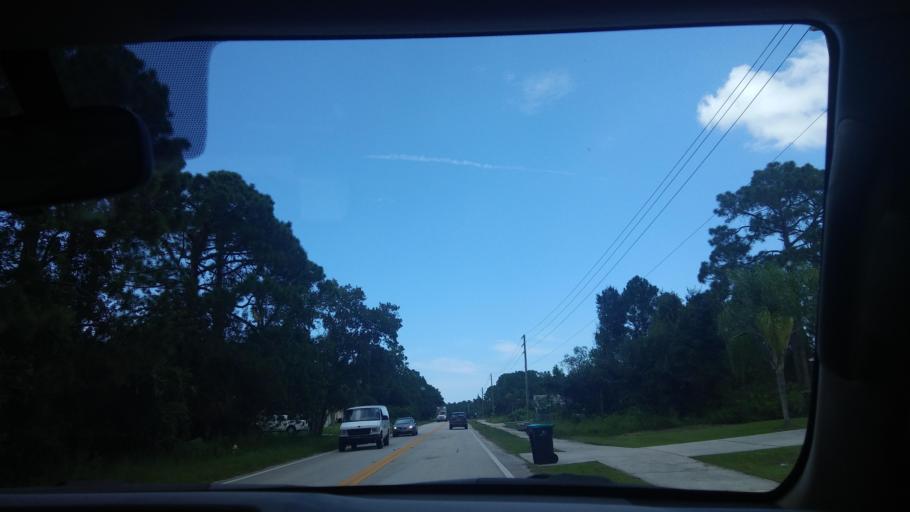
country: US
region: Florida
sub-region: Brevard County
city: Grant-Valkaria
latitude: 27.9662
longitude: -80.6291
